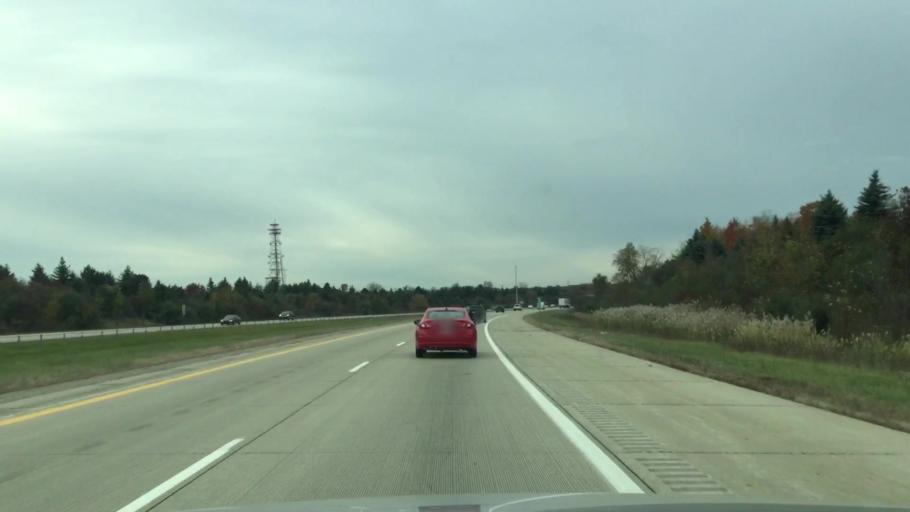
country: US
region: Michigan
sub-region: Wayne County
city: Plymouth
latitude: 42.3708
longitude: -83.5402
